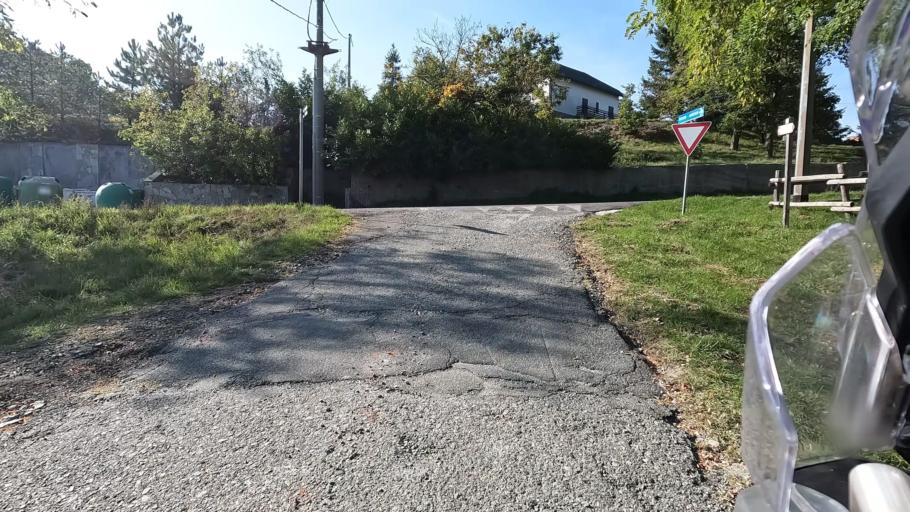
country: IT
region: Liguria
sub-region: Provincia di Savona
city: Sassello
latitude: 44.5281
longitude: 8.5332
